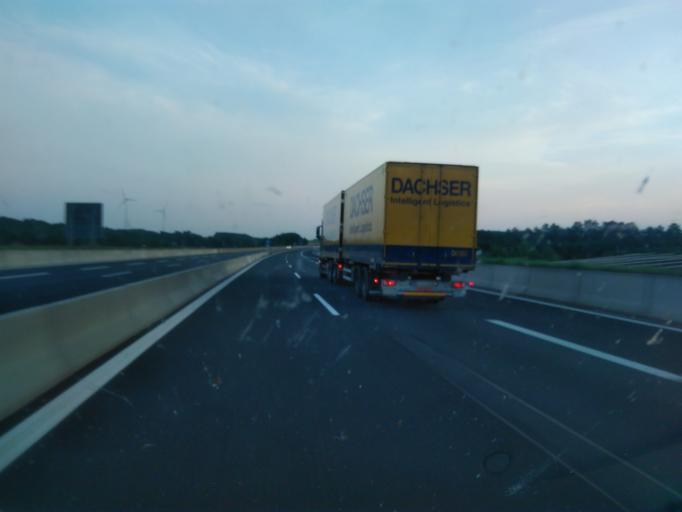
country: DE
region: Bavaria
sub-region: Regierungsbezirk Unterfranken
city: Rannungen
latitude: 50.1975
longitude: 10.2149
